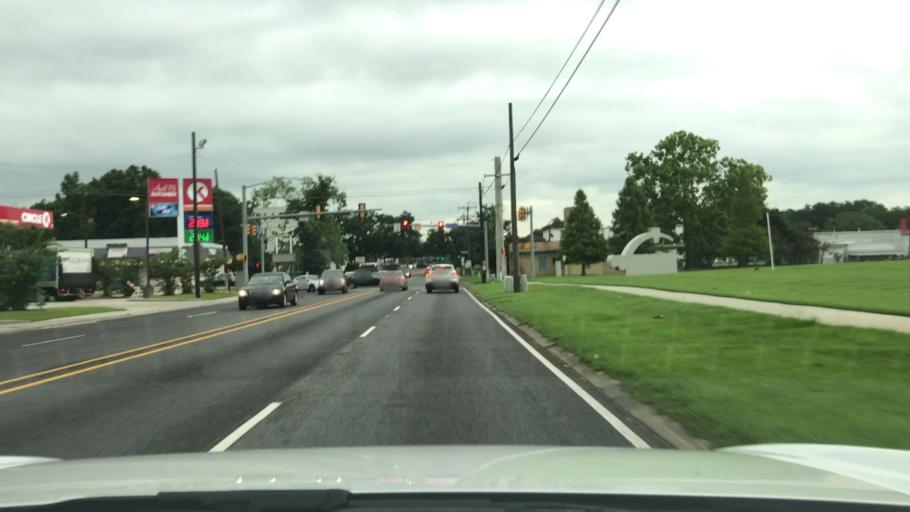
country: US
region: Louisiana
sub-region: East Baton Rouge Parish
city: Baton Rouge
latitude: 30.4480
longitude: -91.1388
